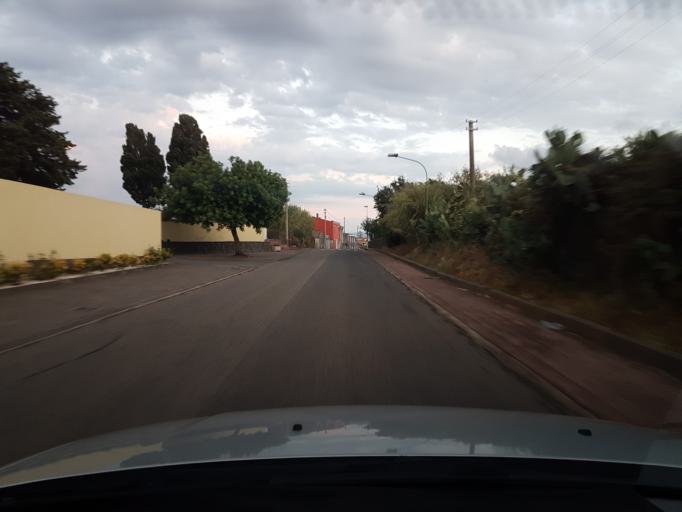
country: IT
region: Sardinia
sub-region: Provincia di Oristano
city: Tramatza
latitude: 40.0064
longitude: 8.6475
